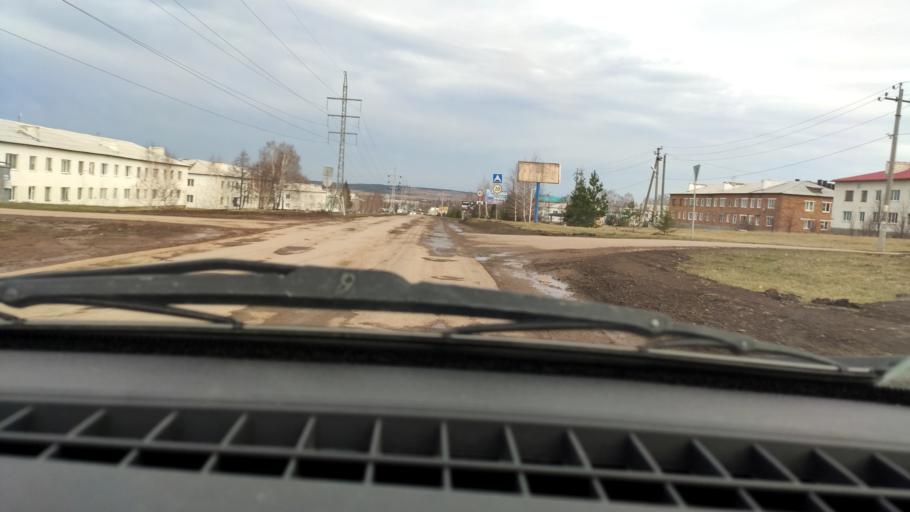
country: RU
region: Bashkortostan
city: Davlekanovo
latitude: 54.2264
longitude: 55.0370
